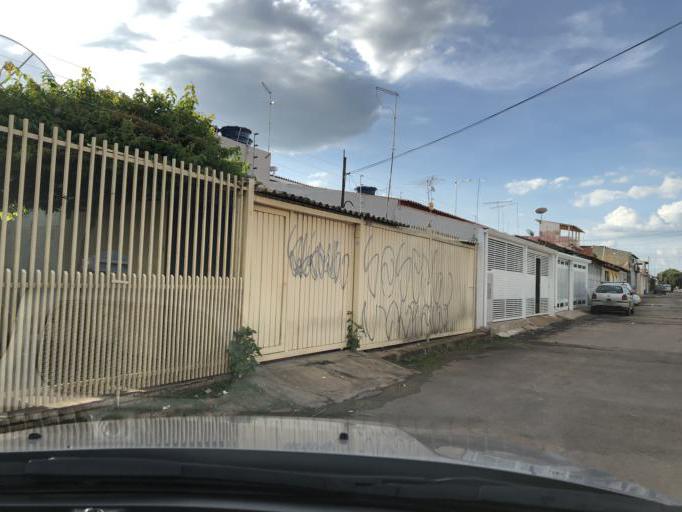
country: BR
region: Federal District
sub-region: Brasilia
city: Brasilia
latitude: -15.8084
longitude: -48.1351
